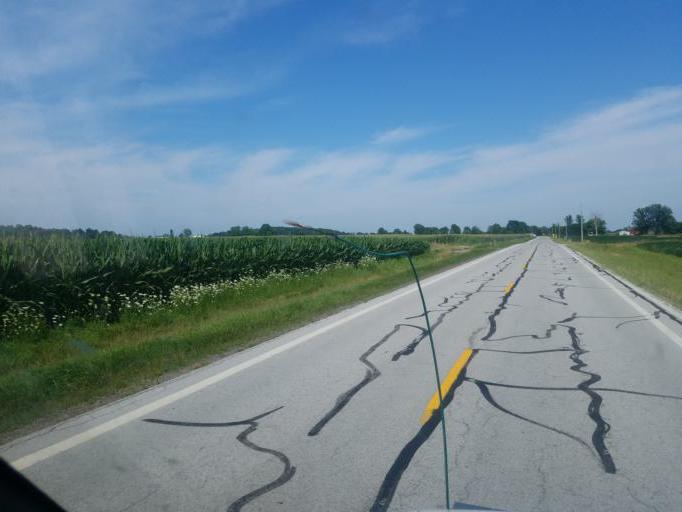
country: US
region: Ohio
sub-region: Logan County
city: Lakeview
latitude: 40.6012
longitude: -83.8909
